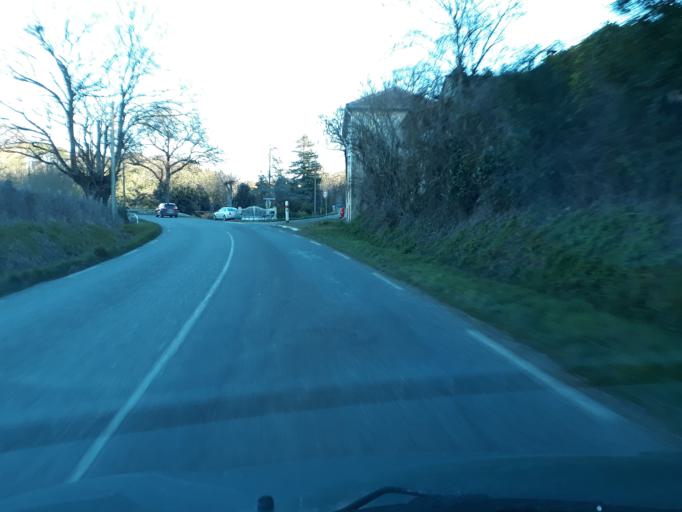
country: FR
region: Midi-Pyrenees
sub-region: Departement du Gers
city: Pavie
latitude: 43.6300
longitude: 0.6162
